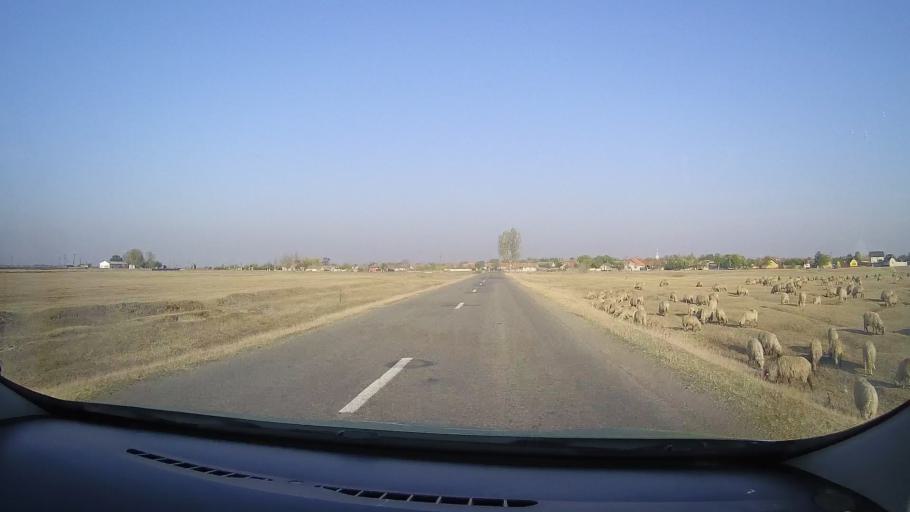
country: RO
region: Arad
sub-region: Comuna Graniceri
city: Graniceri
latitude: 46.5130
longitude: 21.3090
